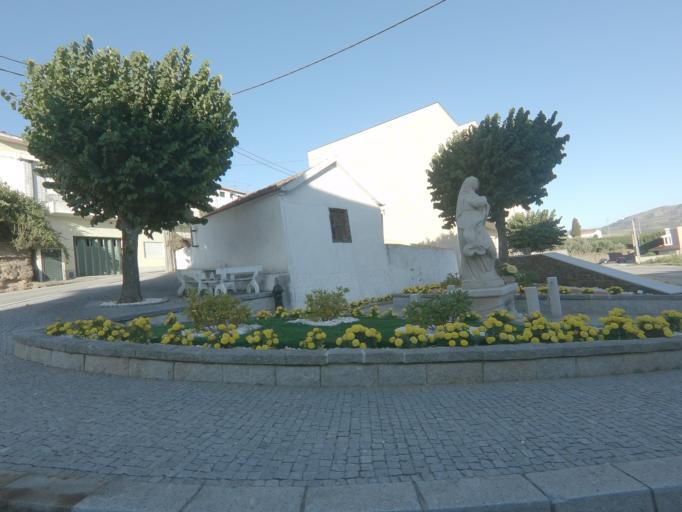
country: PT
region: Vila Real
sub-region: Peso da Regua
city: Godim
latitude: 41.1630
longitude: -7.8191
